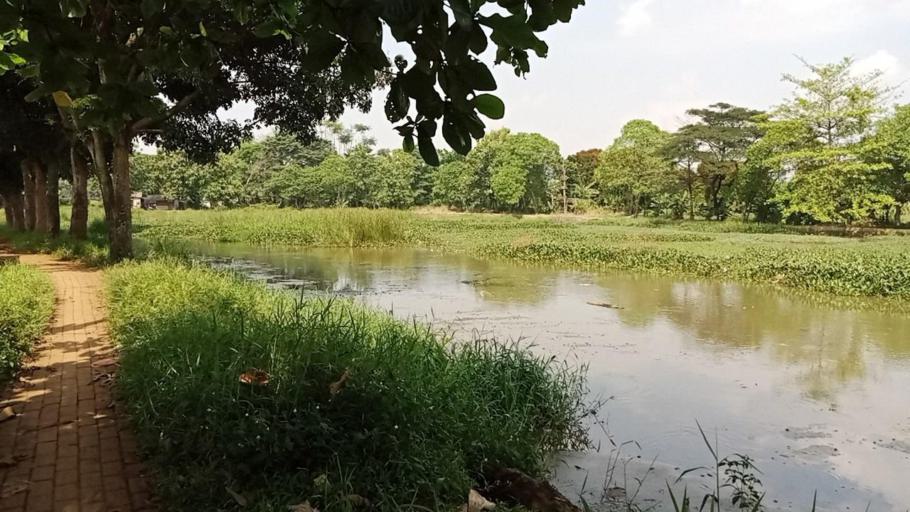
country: ID
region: West Java
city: Parung
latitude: -6.4221
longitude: 106.7487
